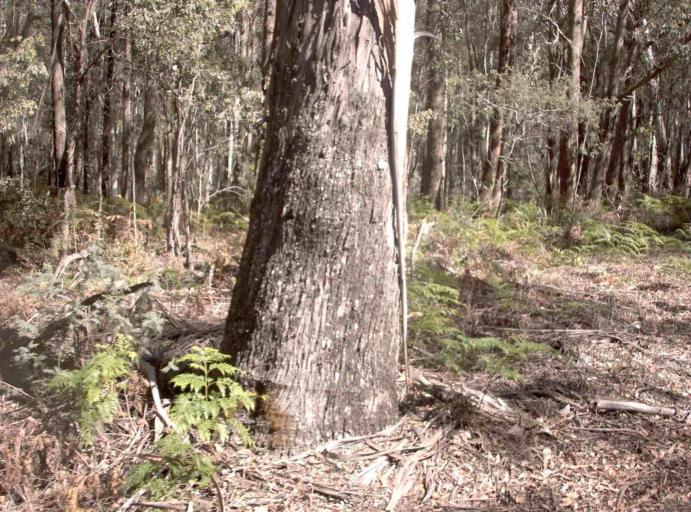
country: AU
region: New South Wales
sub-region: Bombala
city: Bombala
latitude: -37.1175
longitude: 148.7534
